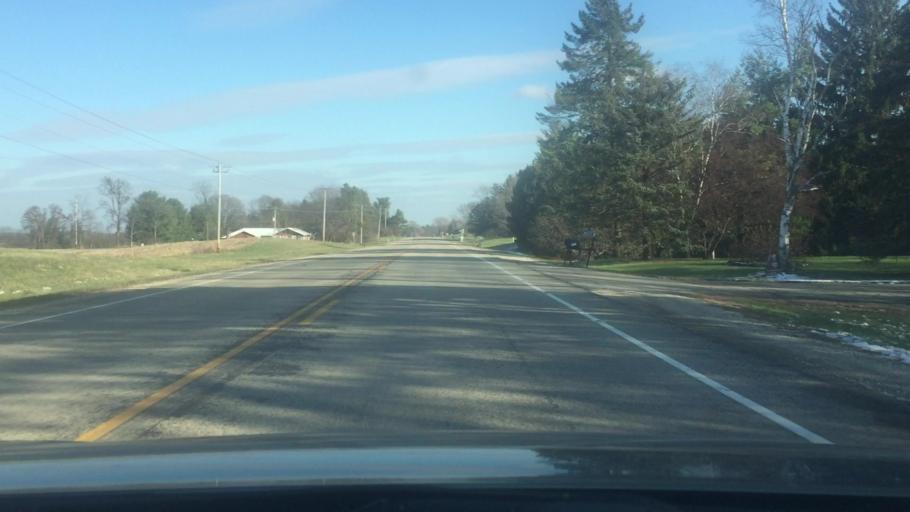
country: US
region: Wisconsin
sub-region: Jefferson County
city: Fort Atkinson
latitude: 42.9393
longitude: -88.7818
